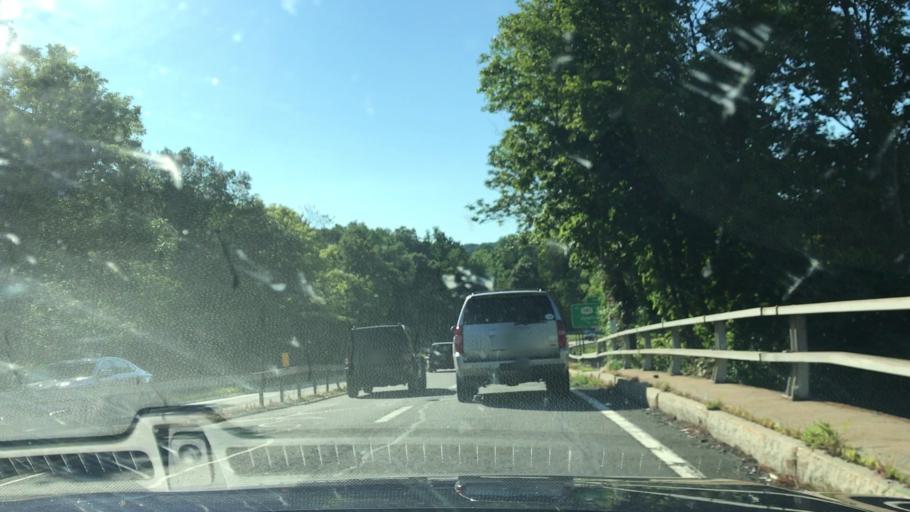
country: US
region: New York
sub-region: Westchester County
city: Hawthorne
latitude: 41.0972
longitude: -73.7942
